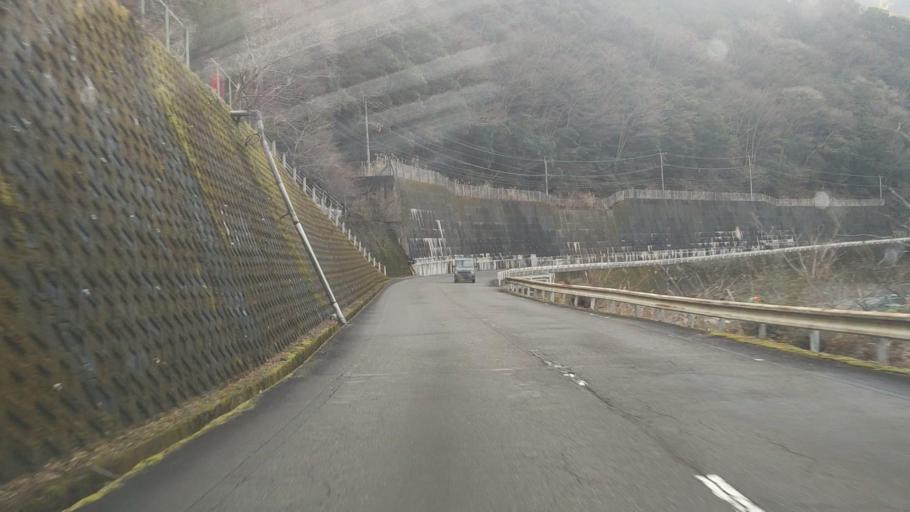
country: JP
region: Kumamoto
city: Hitoyoshi
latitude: 32.4226
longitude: 130.8551
